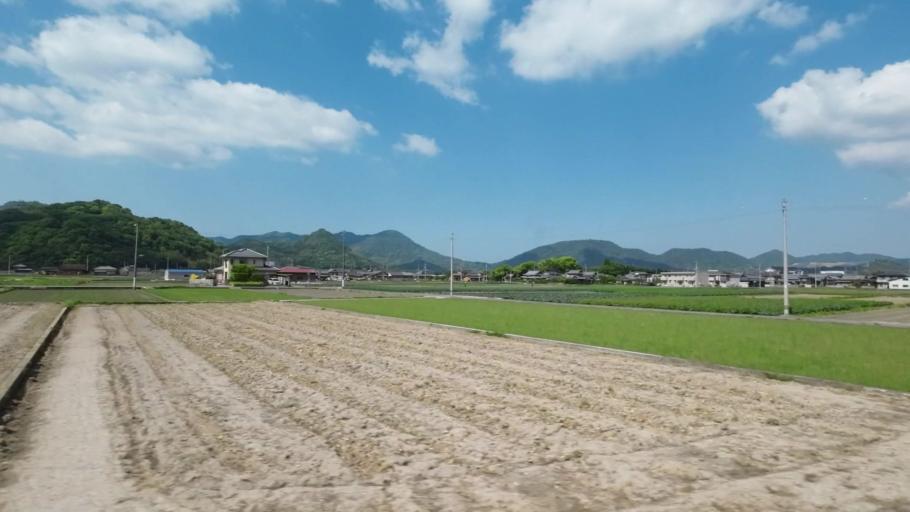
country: JP
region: Kagawa
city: Tadotsu
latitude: 34.2013
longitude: 133.7124
